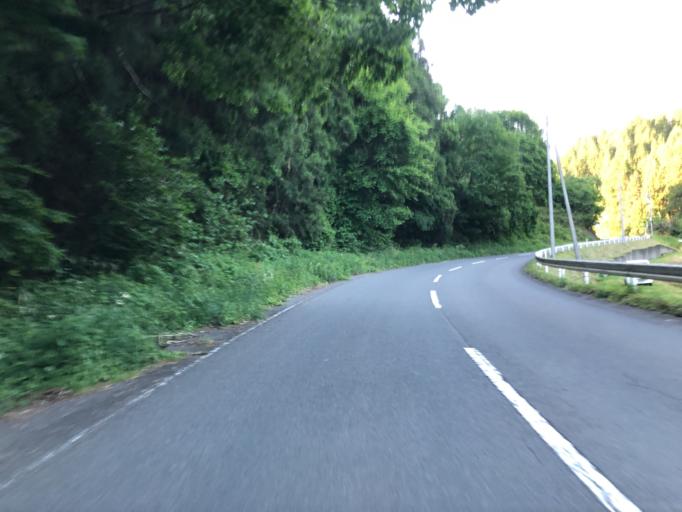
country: JP
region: Fukushima
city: Ishikawa
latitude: 37.0055
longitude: 140.4347
